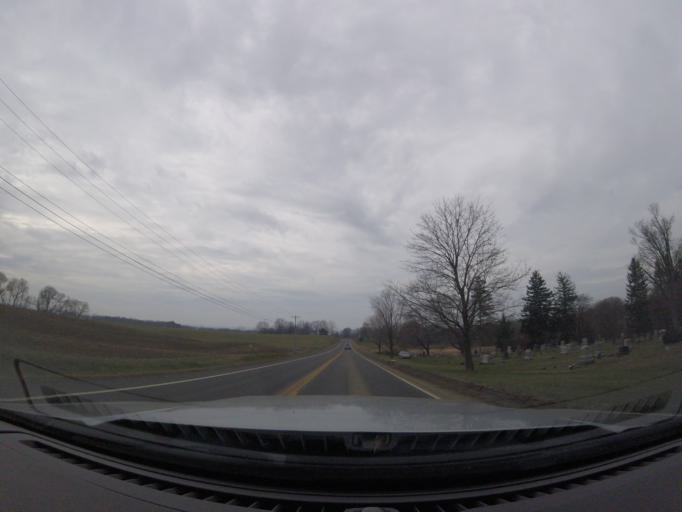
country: US
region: New York
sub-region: Schuyler County
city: Watkins Glen
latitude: 42.4238
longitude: -76.8240
